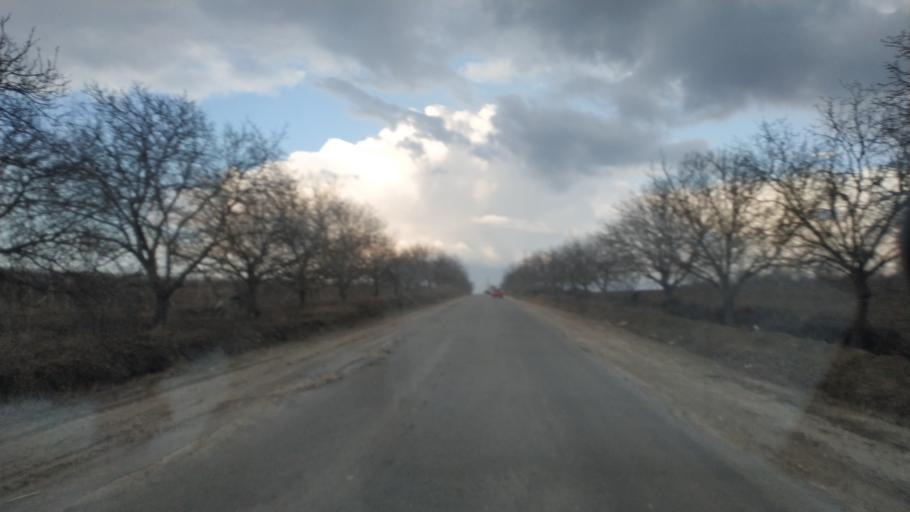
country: MD
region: Anenii Noi
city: Anenii Noi
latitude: 46.9587
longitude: 29.2838
